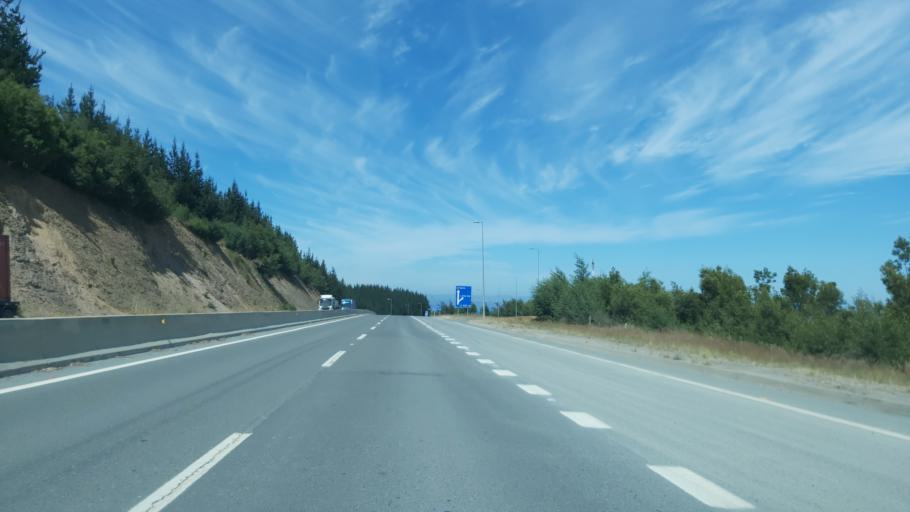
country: CL
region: Biobio
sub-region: Provincia de Concepcion
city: Lota
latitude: -37.0972
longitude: -73.1413
